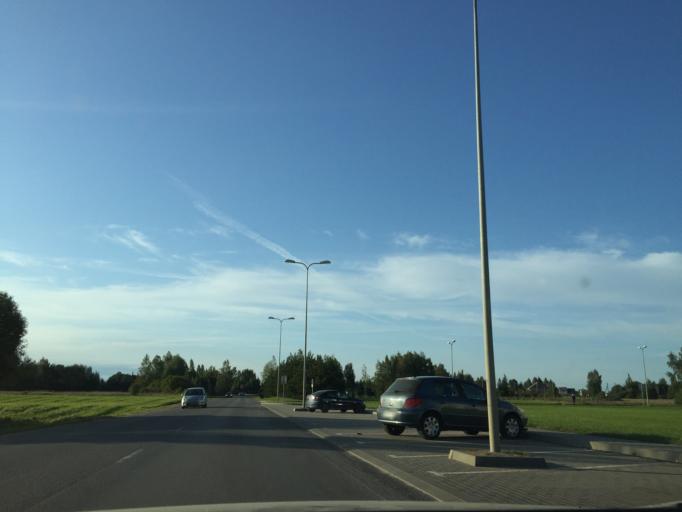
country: LT
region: Panevezys
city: Rokiskis
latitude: 55.9488
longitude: 25.5775
